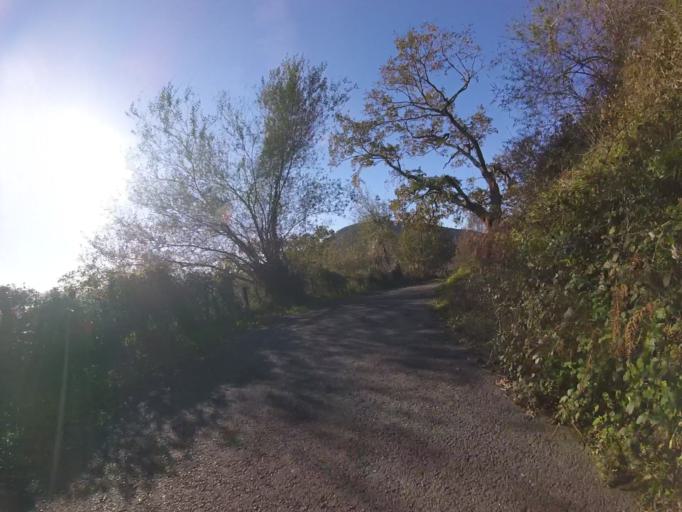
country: ES
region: Basque Country
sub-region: Provincia de Guipuzcoa
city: Usurbil
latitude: 43.3004
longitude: -2.0504
